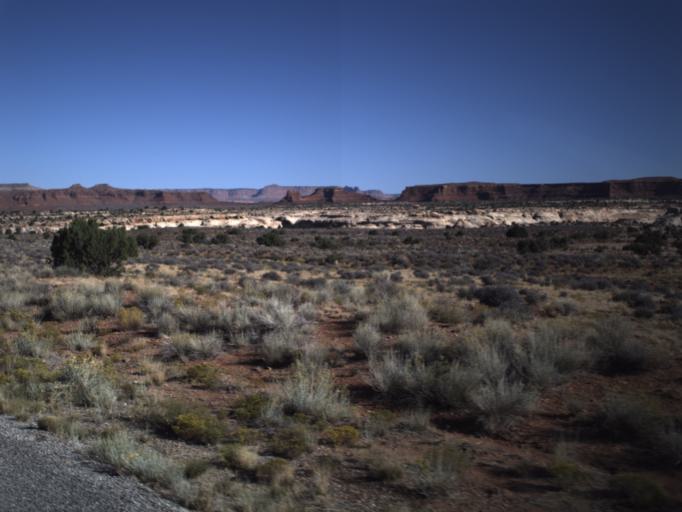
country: US
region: Utah
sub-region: San Juan County
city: Blanding
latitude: 37.7902
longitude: -110.2987
